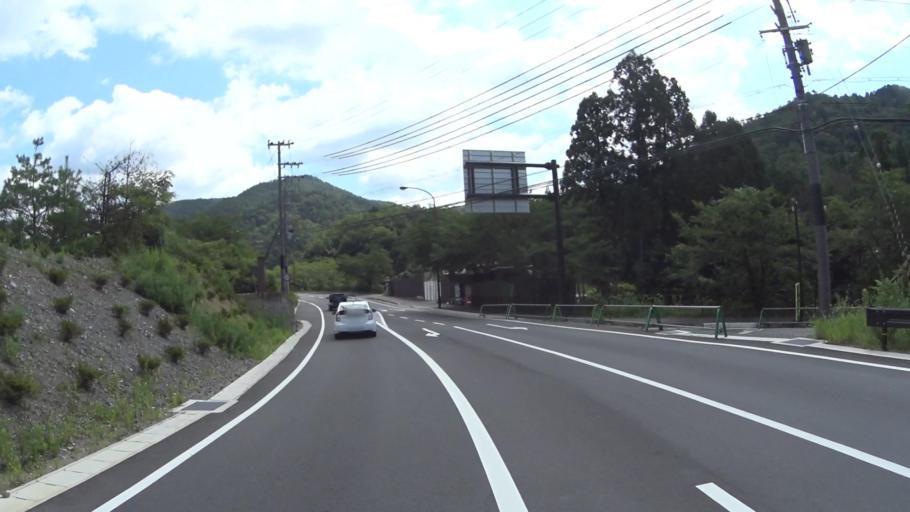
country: JP
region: Kyoto
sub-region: Kyoto-shi
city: Kamigyo-ku
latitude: 35.0937
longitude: 135.7664
